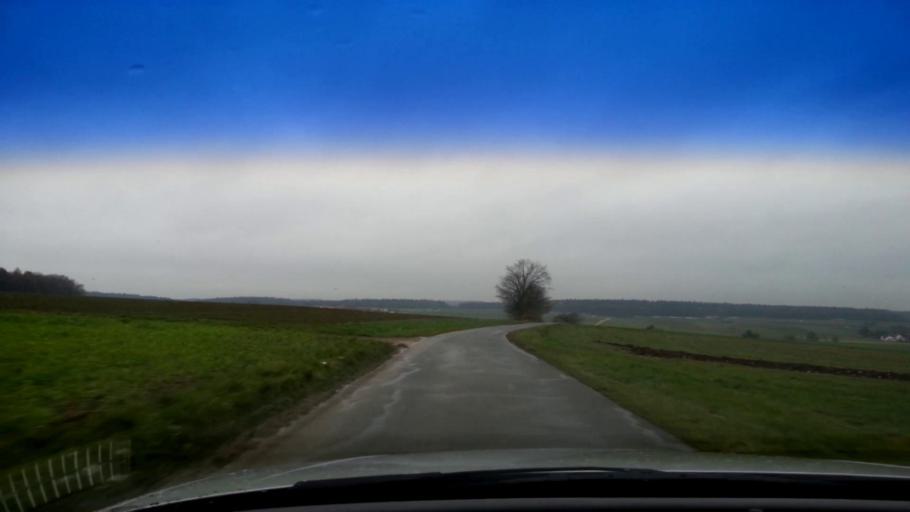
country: DE
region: Bavaria
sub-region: Upper Franconia
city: Memmelsdorf
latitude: 49.9509
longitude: 10.9486
